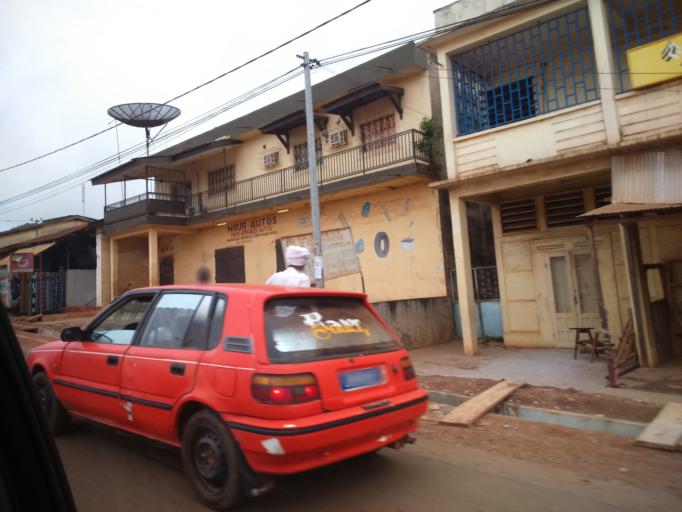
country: CI
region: Moyen-Comoe
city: Abengourou
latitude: 6.7286
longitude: -3.4937
